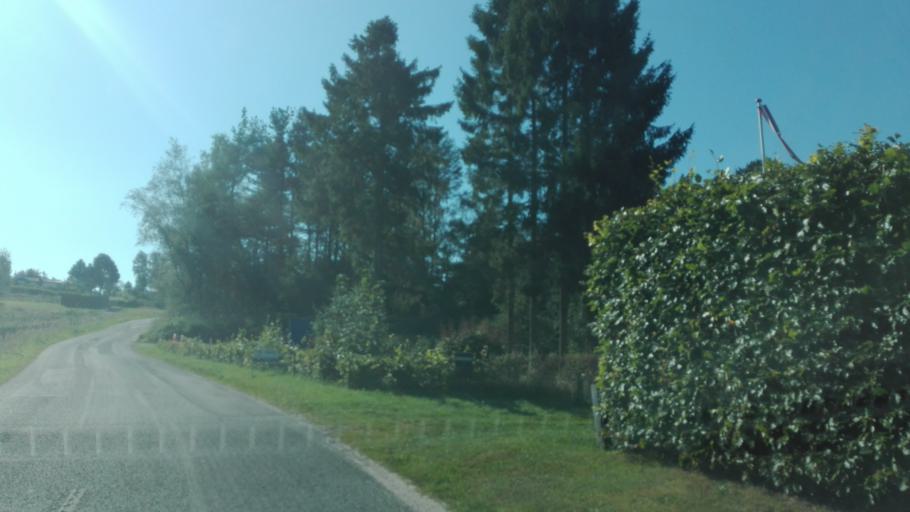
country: DK
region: Central Jutland
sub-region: Syddjurs Kommune
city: Ebeltoft
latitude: 56.2493
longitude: 10.6239
